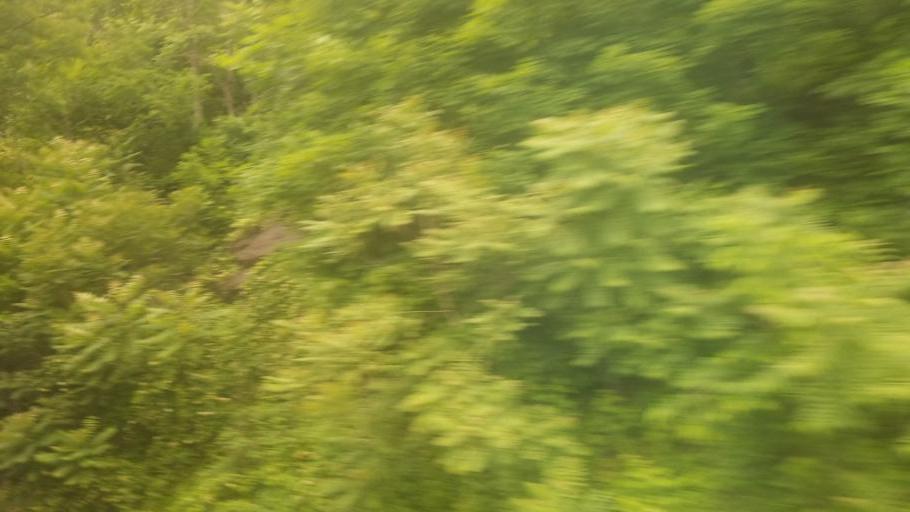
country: US
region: West Virginia
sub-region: Morgan County
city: Berkeley Springs
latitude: 39.6087
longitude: -78.3730
